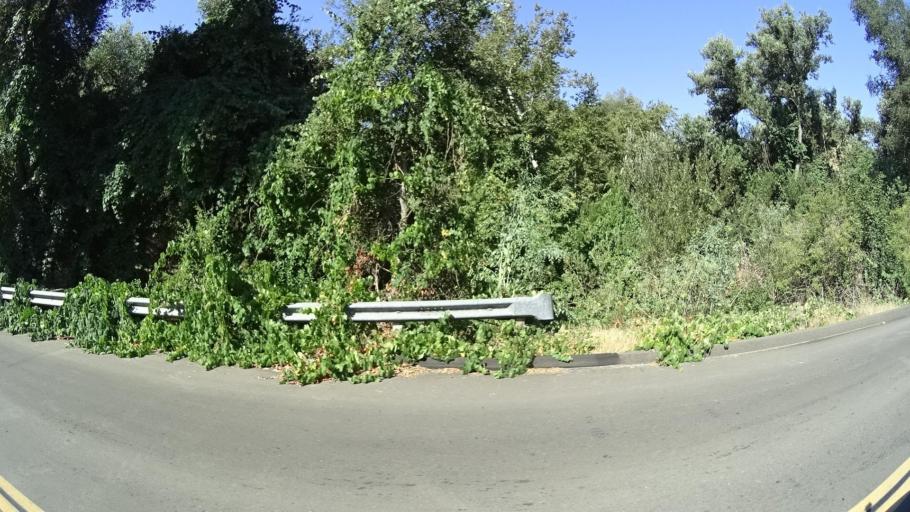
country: US
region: California
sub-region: San Diego County
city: Rainbow
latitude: 33.4078
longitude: -117.2026
